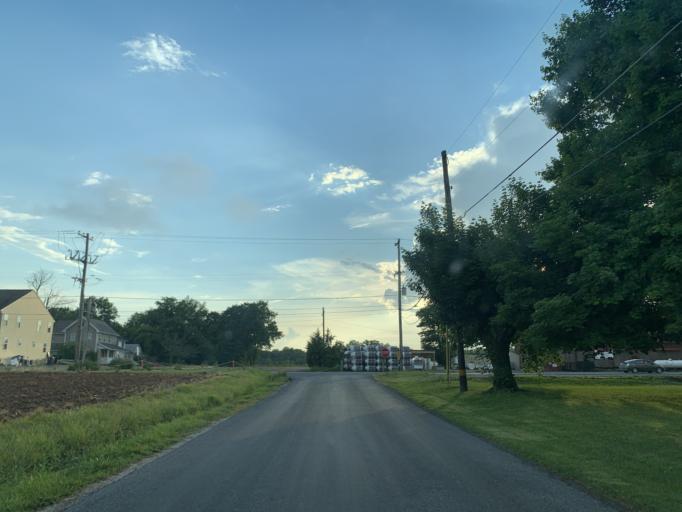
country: US
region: Maryland
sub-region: Cecil County
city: Rising Sun
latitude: 39.7218
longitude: -76.0271
